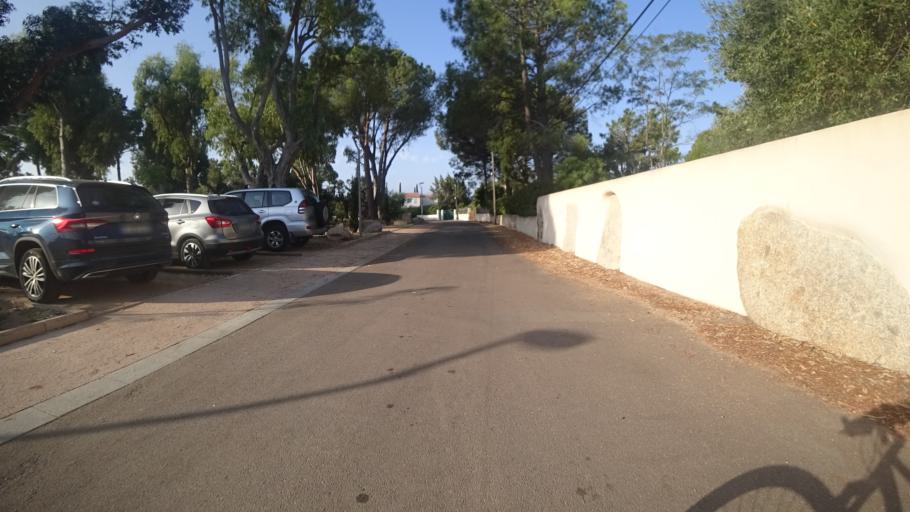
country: FR
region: Corsica
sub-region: Departement de la Corse-du-Sud
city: Porto-Vecchio
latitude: 41.6361
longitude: 9.3436
